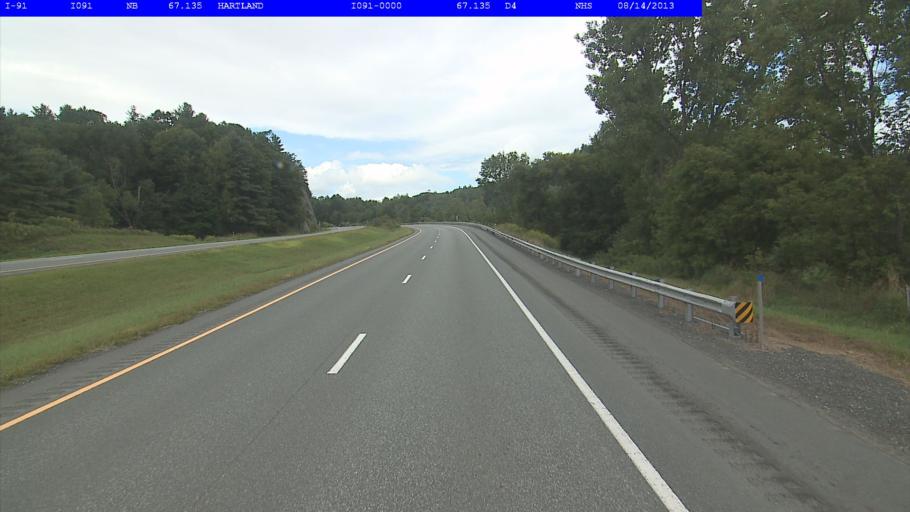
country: US
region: Vermont
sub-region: Windsor County
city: White River Junction
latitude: 43.6031
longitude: -72.3422
